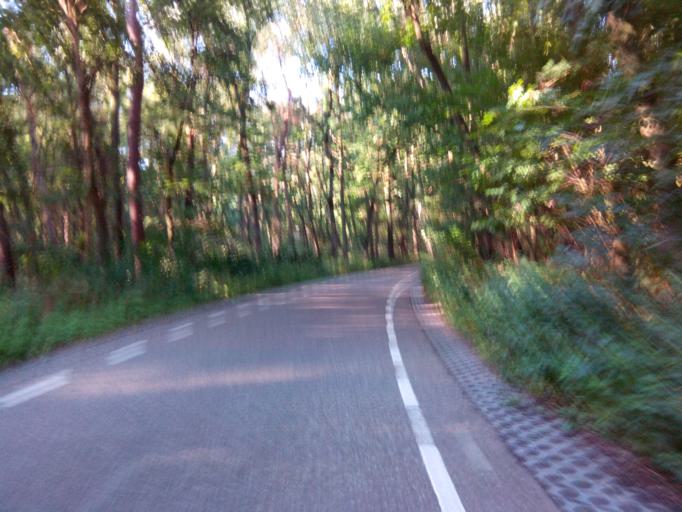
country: NL
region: Utrecht
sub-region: Gemeente Utrechtse Heuvelrug
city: Amerongen
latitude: 52.0291
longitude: 5.4616
